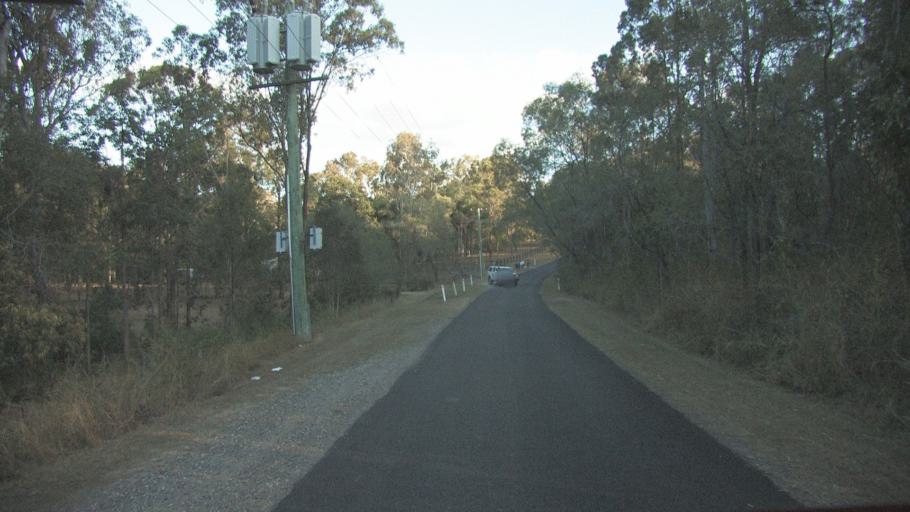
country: AU
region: Queensland
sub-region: Logan
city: Cedar Vale
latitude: -27.8467
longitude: 153.0831
